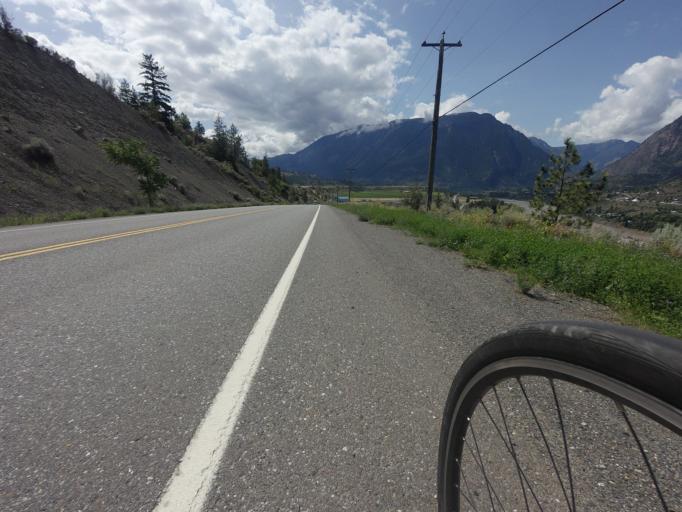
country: CA
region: British Columbia
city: Lillooet
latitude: 50.7092
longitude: -121.9086
